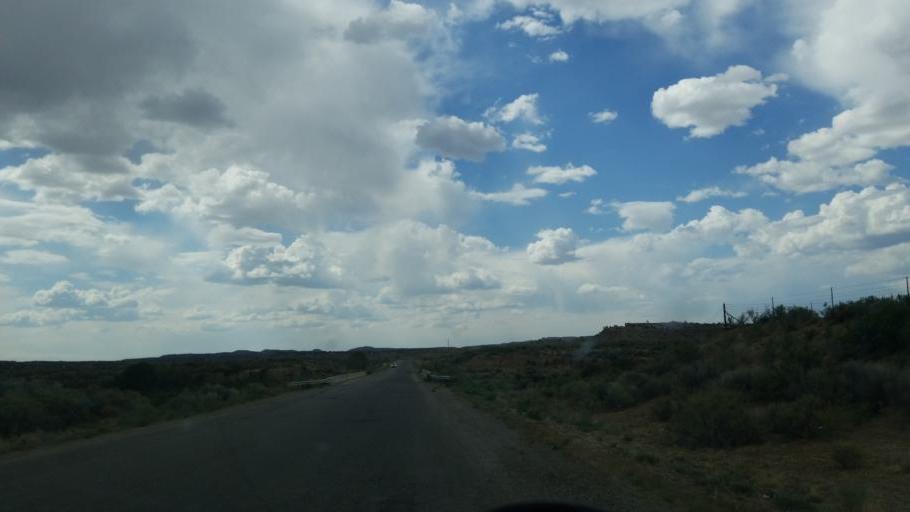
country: US
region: New Mexico
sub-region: McKinley County
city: Gallup
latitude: 35.4896
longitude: -108.9047
